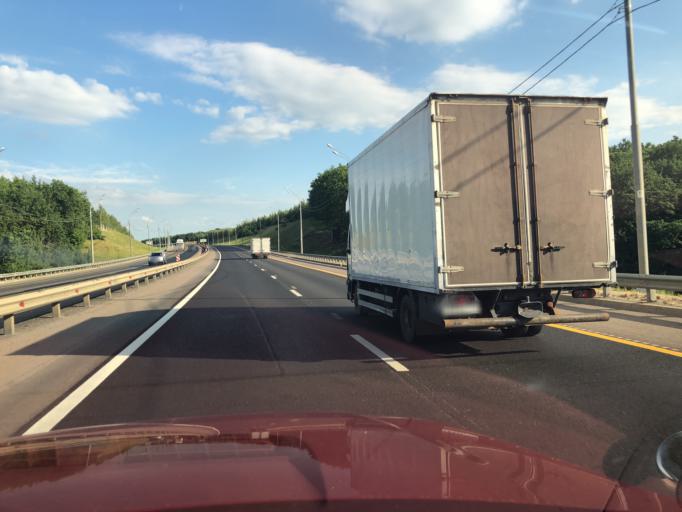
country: RU
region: Lipetsk
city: Zadonsk
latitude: 52.3928
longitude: 38.8629
